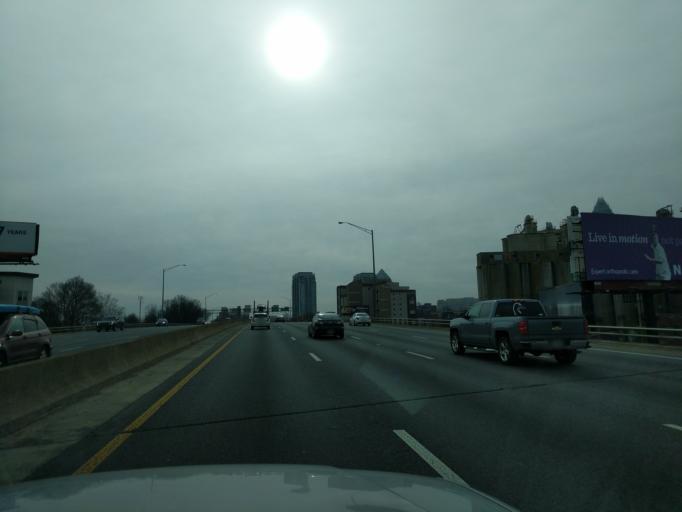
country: US
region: North Carolina
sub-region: Mecklenburg County
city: Charlotte
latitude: 35.2386
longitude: -80.8415
